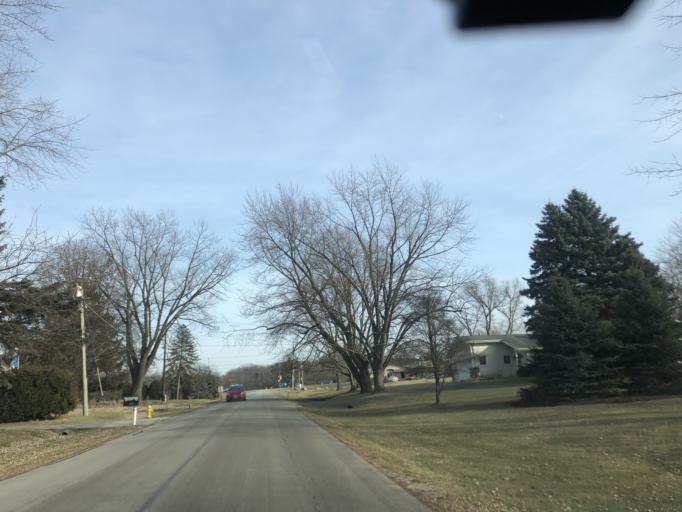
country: US
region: Illinois
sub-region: Cook County
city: Lemont
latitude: 41.7110
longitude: -88.0092
